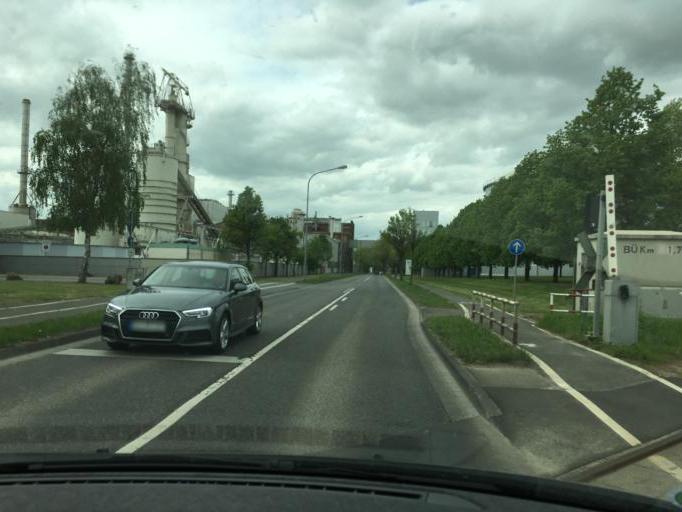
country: DE
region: North Rhine-Westphalia
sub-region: Regierungsbezirk Koln
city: Euskirchen
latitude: 50.6572
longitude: 6.8134
